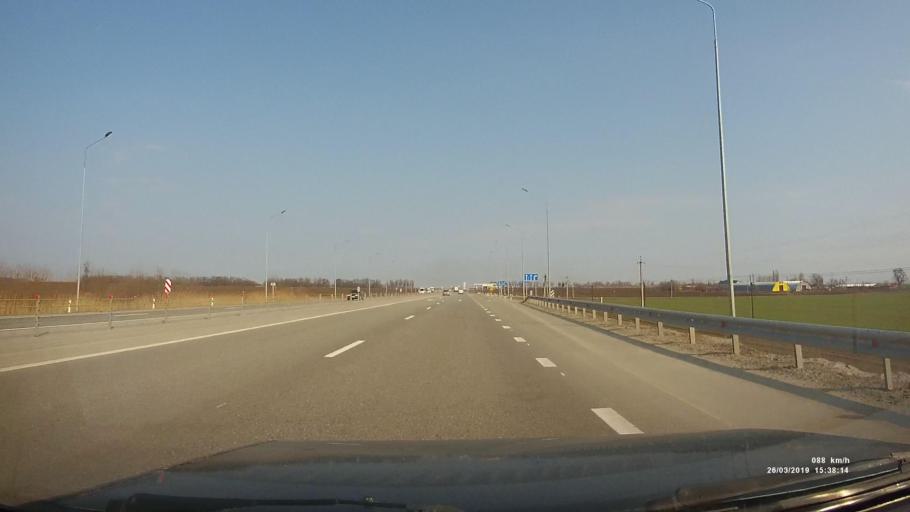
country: RU
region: Rostov
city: Sinyavskoye
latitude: 47.2939
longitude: 39.2674
